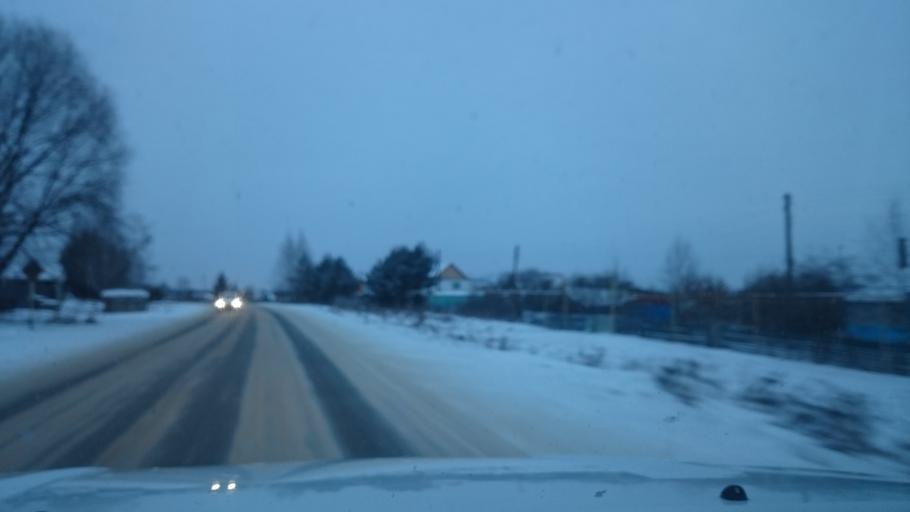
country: RU
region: Tula
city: Leninskiy
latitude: 54.2517
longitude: 37.3748
